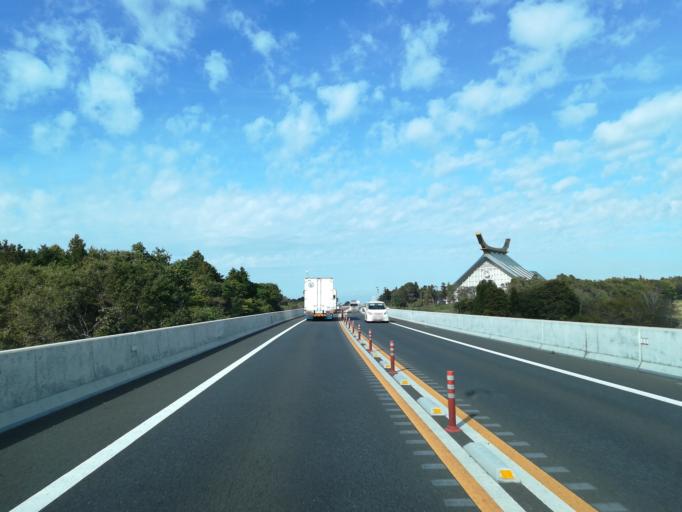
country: JP
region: Ibaraki
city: Mitsukaido
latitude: 36.0728
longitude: 140.0147
